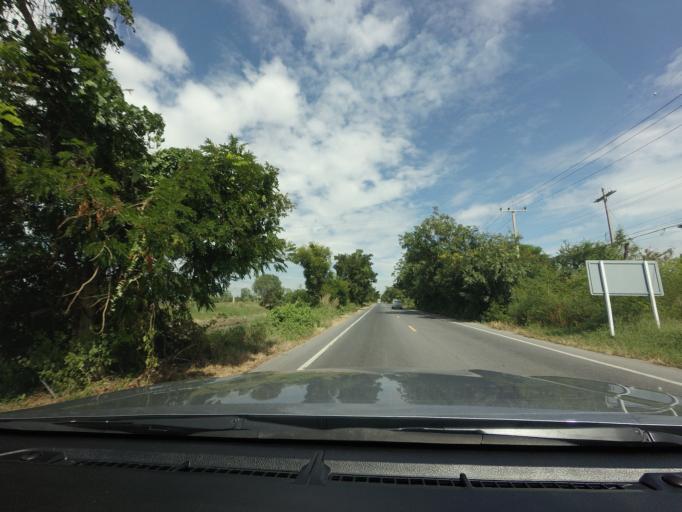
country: TH
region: Suphan Buri
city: Suphan Buri
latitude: 14.4561
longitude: 100.0854
